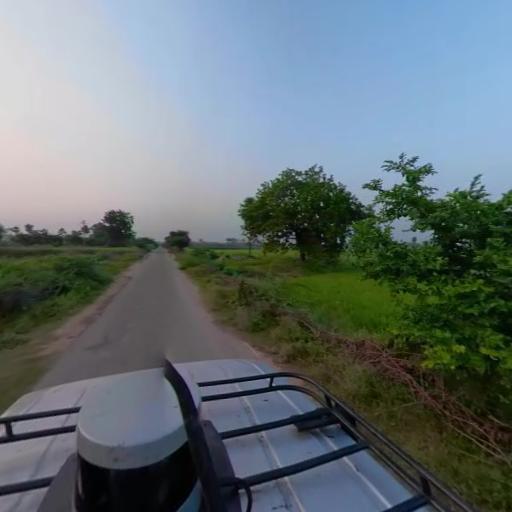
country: IN
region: Telangana
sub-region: Nalgonda
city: Suriapet
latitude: 17.0626
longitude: 79.5472
